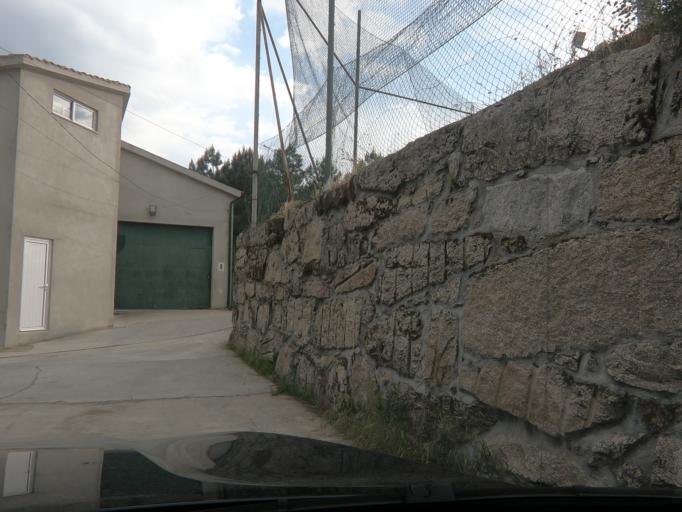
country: PT
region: Vila Real
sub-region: Vila Real
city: Vila Real
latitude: 41.3077
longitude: -7.6965
